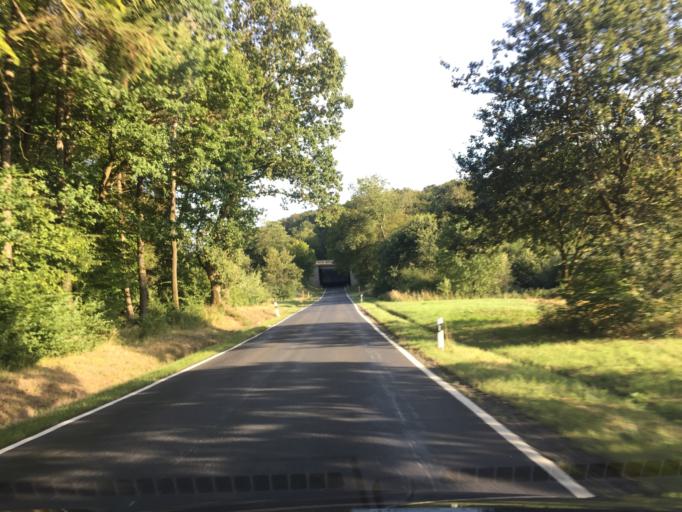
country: DE
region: Rheinland-Pfalz
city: Grossholbach
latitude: 50.4561
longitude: 7.8830
